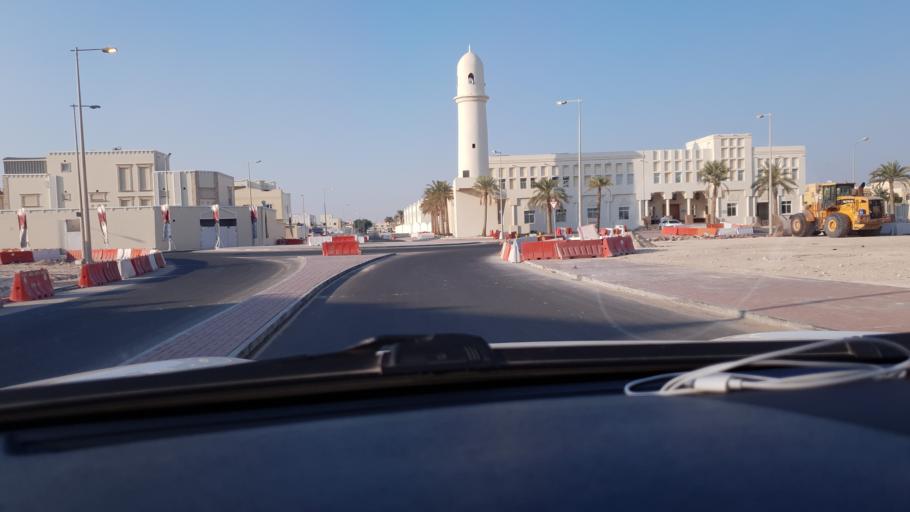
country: QA
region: Baladiyat ad Dawhah
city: Doha
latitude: 25.2351
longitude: 51.5561
